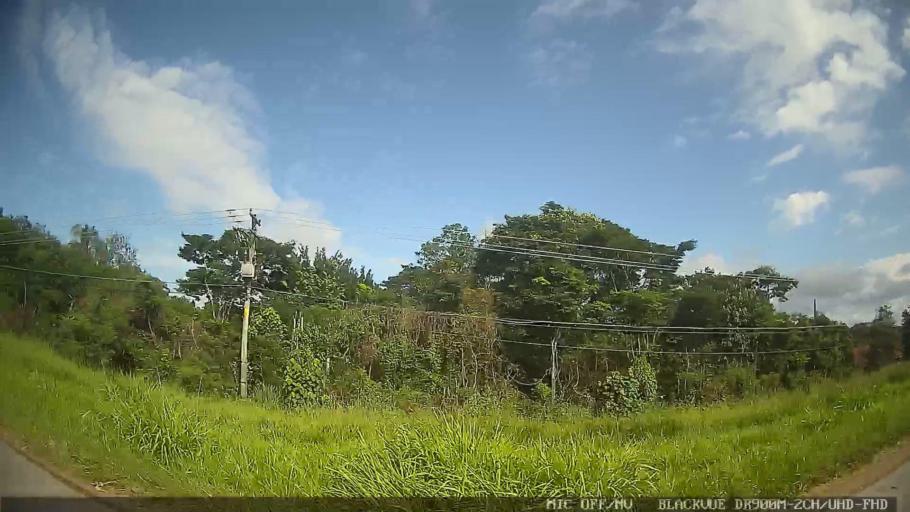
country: BR
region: Sao Paulo
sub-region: Jarinu
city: Jarinu
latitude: -23.0560
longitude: -46.6795
